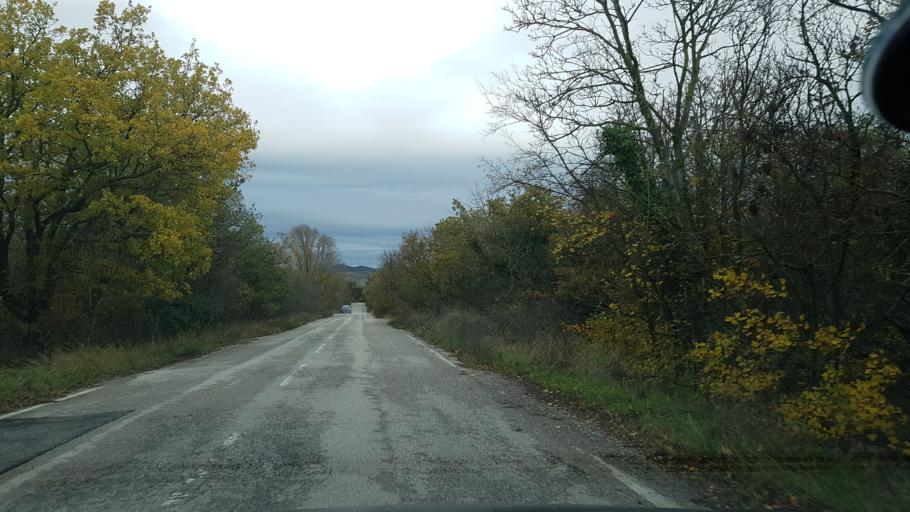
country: IT
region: Friuli Venezia Giulia
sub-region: Provincia di Trieste
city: Prosecco-Contovello
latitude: 45.7014
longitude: 13.7432
